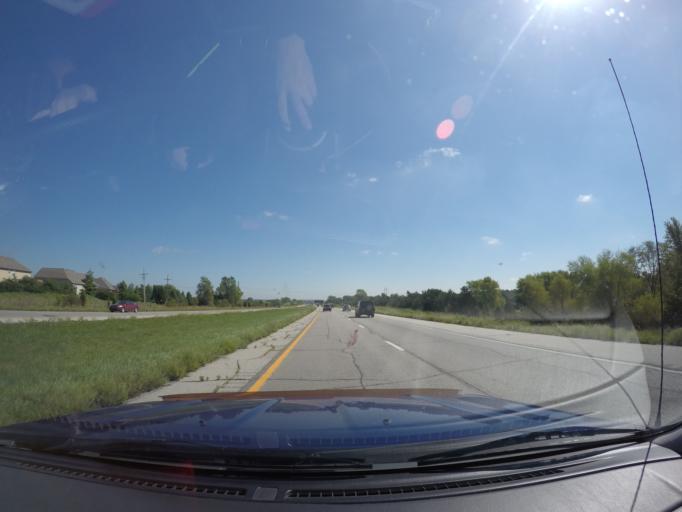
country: US
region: Kansas
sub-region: Johnson County
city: Olathe
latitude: 38.9412
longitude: -94.8318
